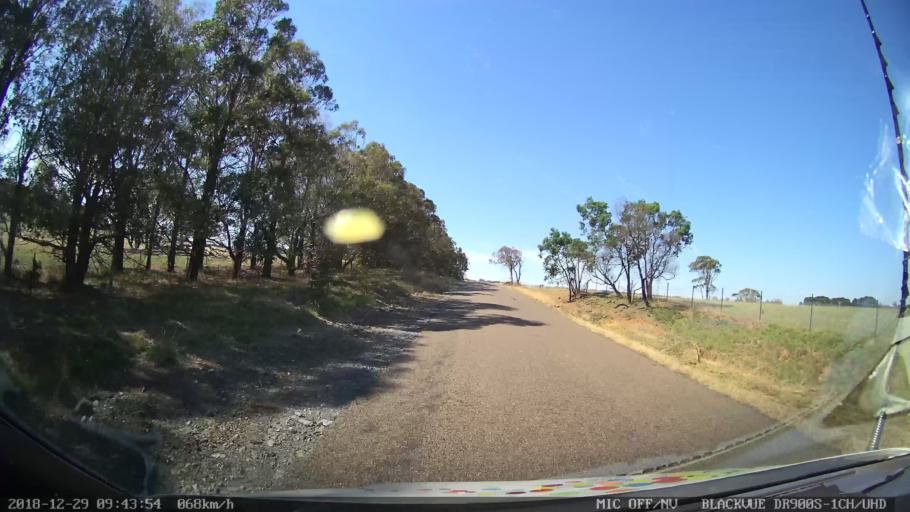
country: AU
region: New South Wales
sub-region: Upper Lachlan Shire
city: Crookwell
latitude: -34.6841
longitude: 149.4251
